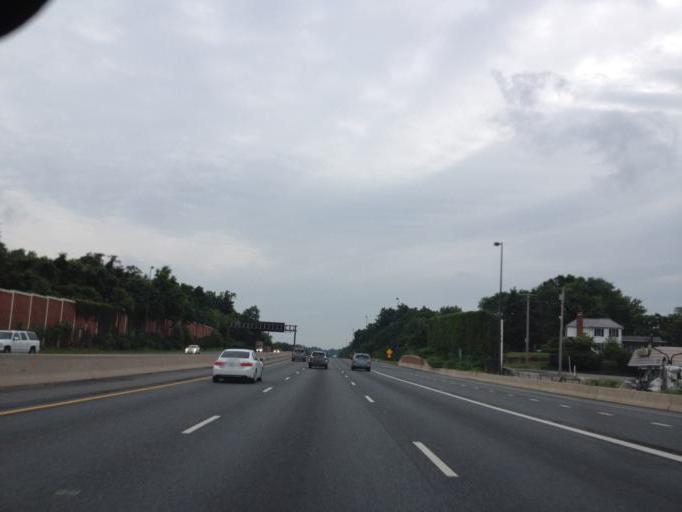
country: US
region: Maryland
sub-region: Anne Arundel County
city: Parole
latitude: 38.9968
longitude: -76.5120
